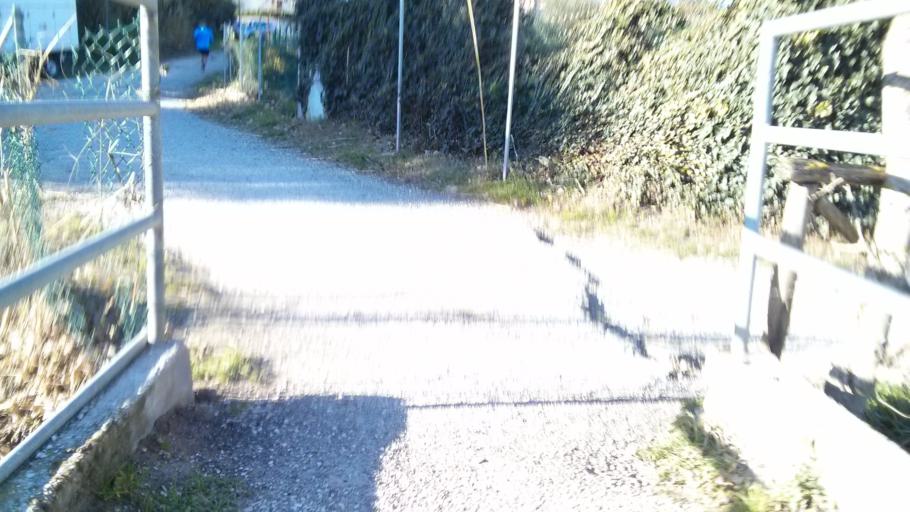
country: IT
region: The Marches
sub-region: Provincia di Pesaro e Urbino
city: Fano
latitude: 43.8523
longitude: 13.0018
